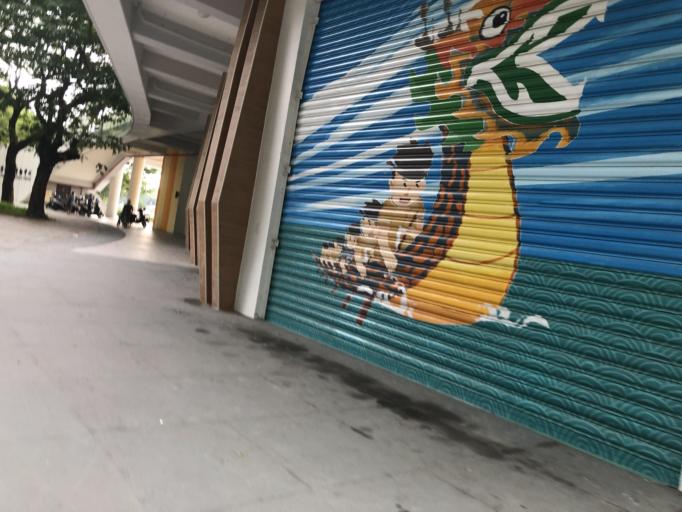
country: TW
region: Kaohsiung
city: Kaohsiung
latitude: 22.6830
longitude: 120.2984
